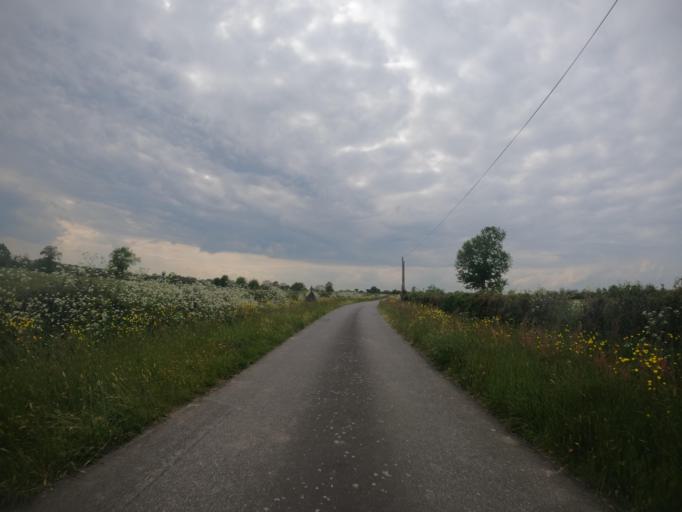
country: FR
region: Poitou-Charentes
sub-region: Departement des Deux-Sevres
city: Chiche
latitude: 46.8546
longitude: -0.3197
